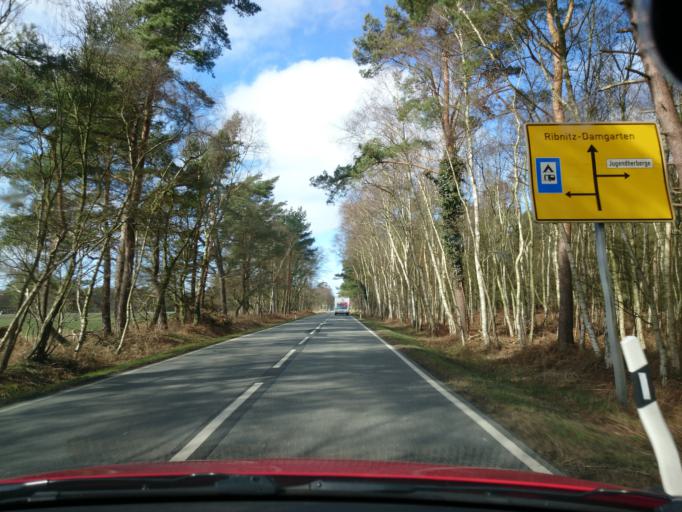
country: DE
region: Mecklenburg-Vorpommern
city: Born
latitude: 54.3980
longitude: 12.4965
